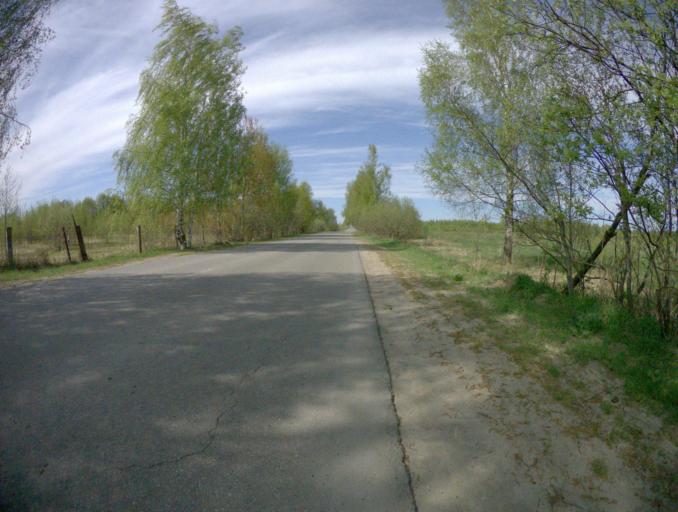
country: RU
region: Vladimir
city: Orgtrud
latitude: 56.1997
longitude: 40.5893
